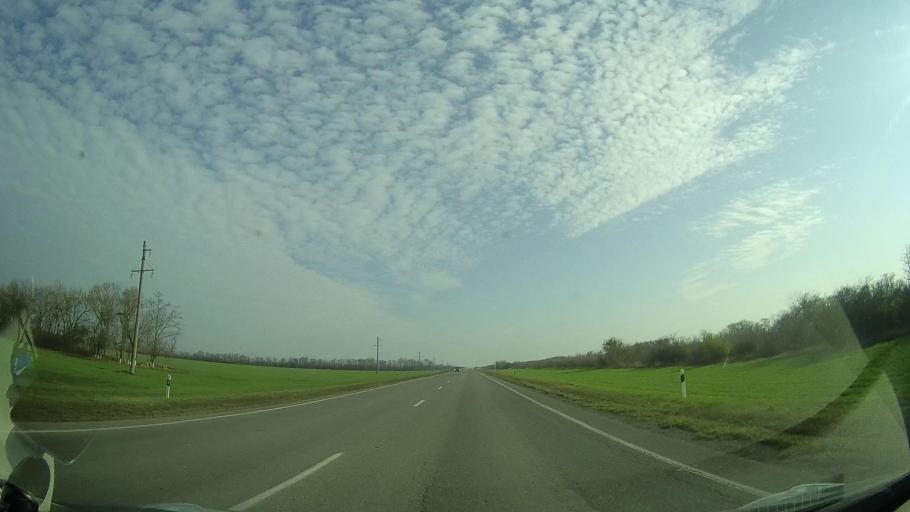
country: RU
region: Rostov
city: Gigant
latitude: 46.5247
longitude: 41.2495
